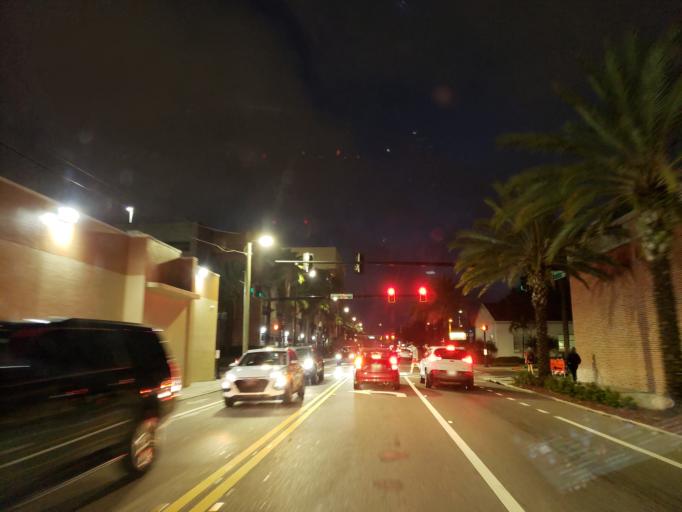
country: US
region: Florida
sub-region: Hillsborough County
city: Tampa
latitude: 27.9468
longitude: -82.4685
